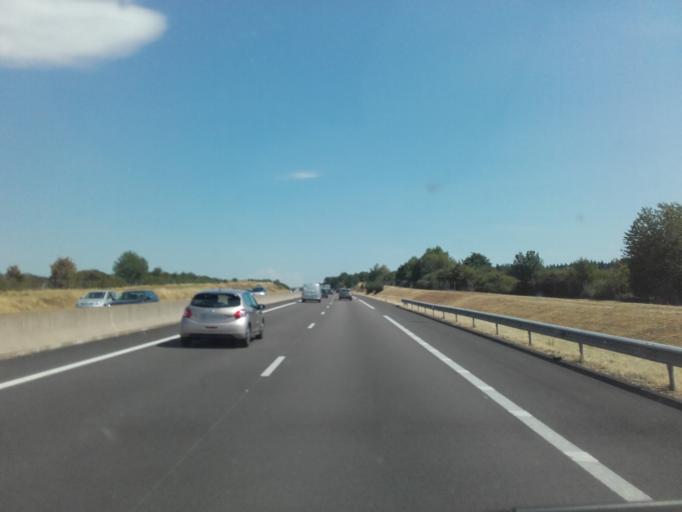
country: FR
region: Bourgogne
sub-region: Departement de la Cote-d'Or
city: Semur-en-Auxois
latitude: 47.3806
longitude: 4.3778
